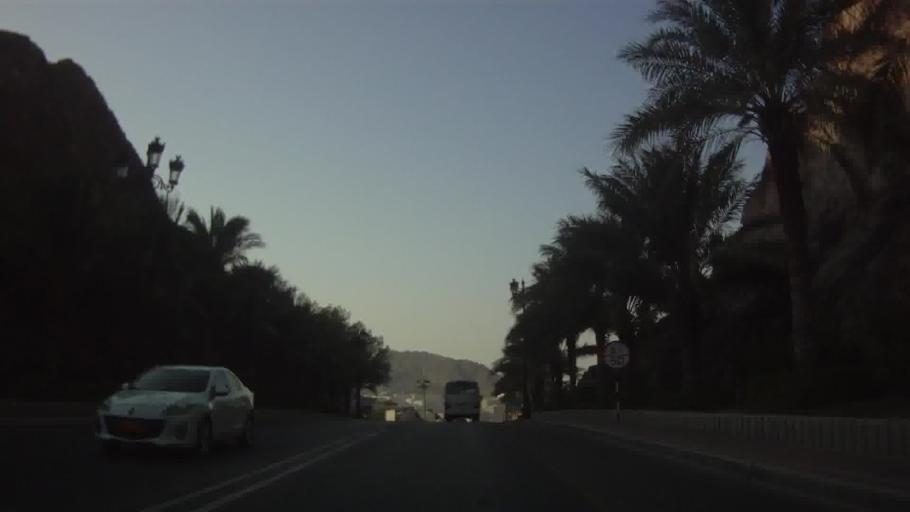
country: OM
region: Muhafazat Masqat
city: Muscat
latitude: 23.6076
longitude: 58.5965
